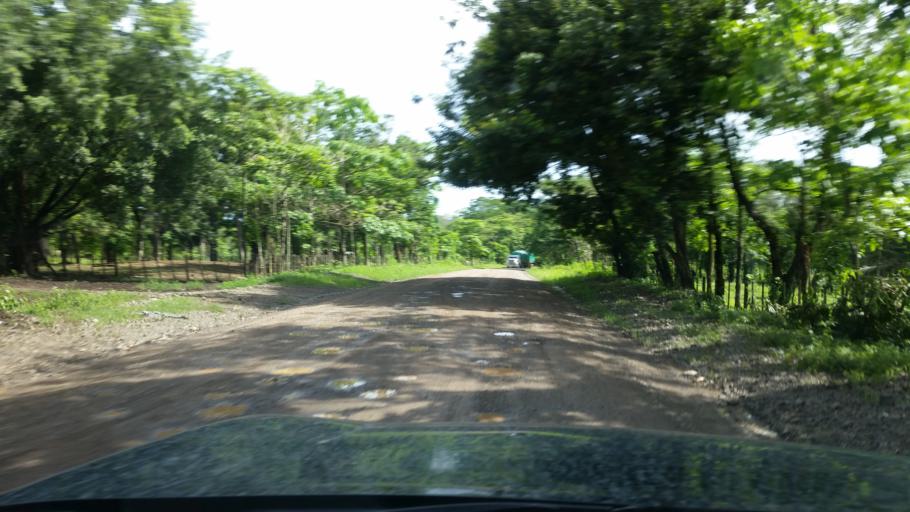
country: NI
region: Atlantico Norte (RAAN)
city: Siuna
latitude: 13.6926
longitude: -84.7865
